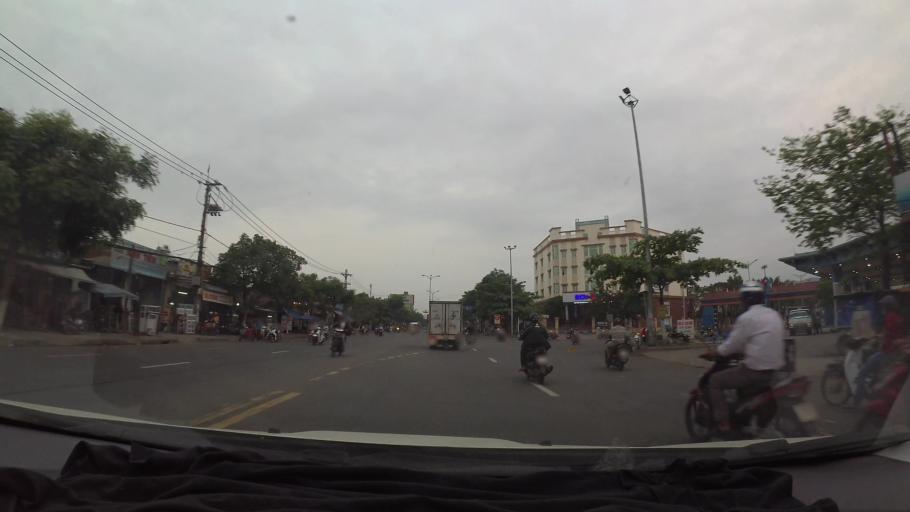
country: VN
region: Da Nang
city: Lien Chieu
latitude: 16.0839
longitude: 108.1455
